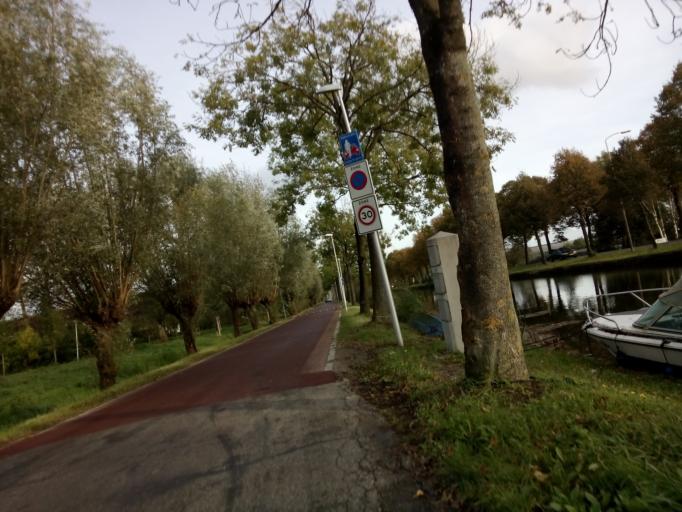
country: NL
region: Utrecht
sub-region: Stichtse Vecht
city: Spechtenkamp
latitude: 52.0904
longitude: 4.9945
